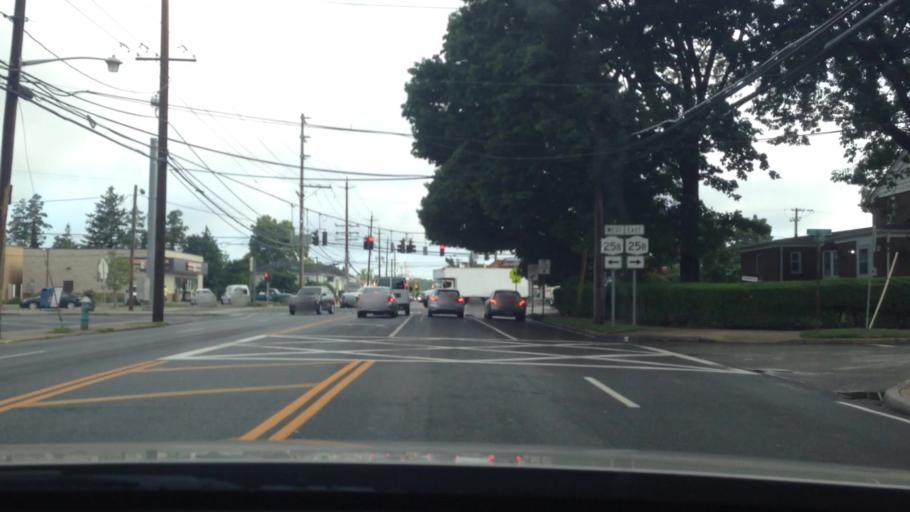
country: US
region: New York
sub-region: Nassau County
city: North New Hyde Park
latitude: 40.7474
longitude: -73.6851
